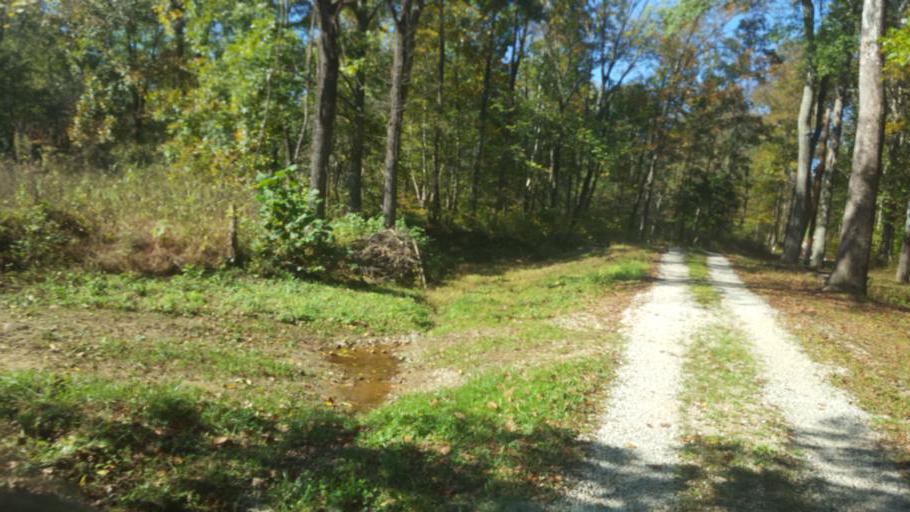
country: US
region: Kentucky
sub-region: Fleming County
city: Flemingsburg
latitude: 38.4600
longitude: -83.5705
